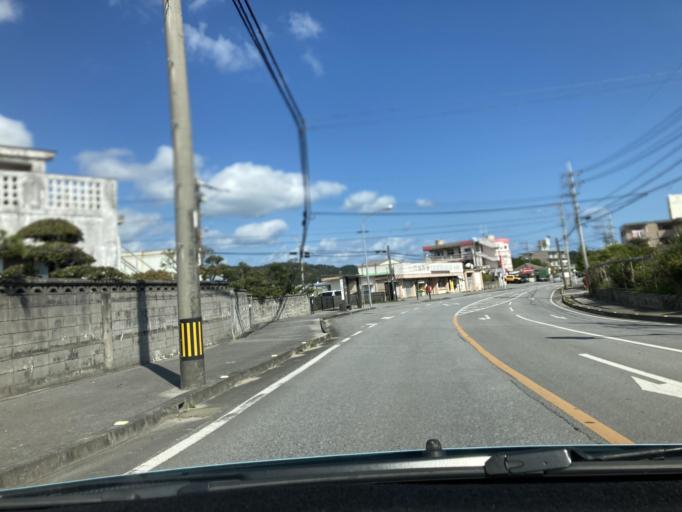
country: JP
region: Okinawa
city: Nago
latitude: 26.6209
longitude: 127.9995
